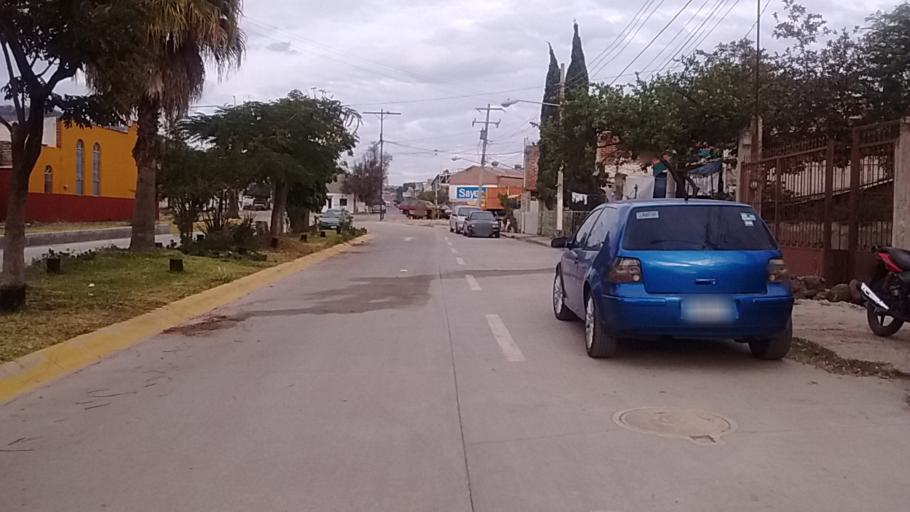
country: MX
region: Jalisco
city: Atotonilco el Alto
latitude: 20.5448
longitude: -102.5149
